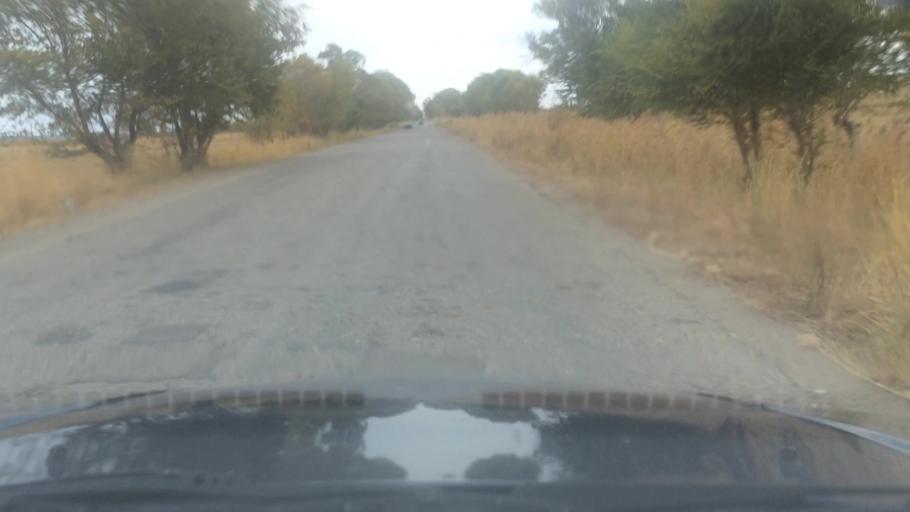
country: KG
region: Ysyk-Koel
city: Balykchy
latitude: 42.3068
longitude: 76.4682
